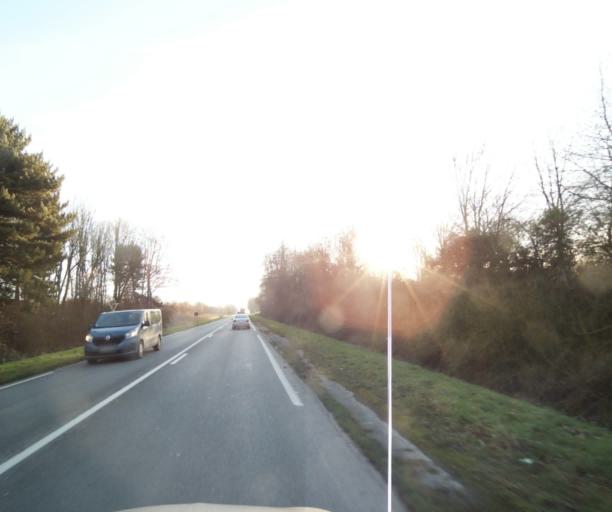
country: FR
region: Nord-Pas-de-Calais
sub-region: Departement du Nord
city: Famars
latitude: 50.3255
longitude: 3.5175
